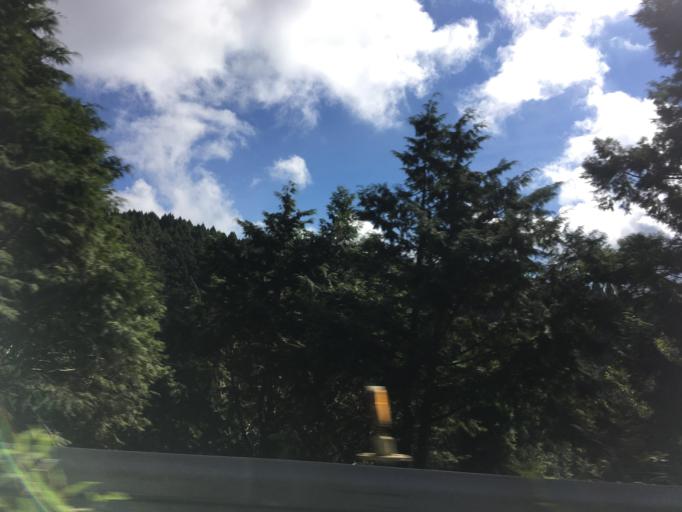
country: TW
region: Taiwan
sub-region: Yilan
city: Yilan
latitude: 24.5132
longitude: 121.5877
